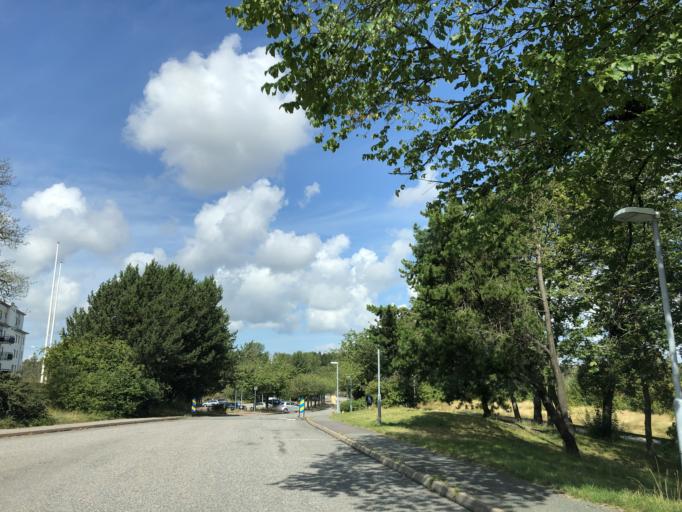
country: SE
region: Vaestra Goetaland
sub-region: Goteborg
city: Majorna
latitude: 57.7034
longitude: 11.9182
